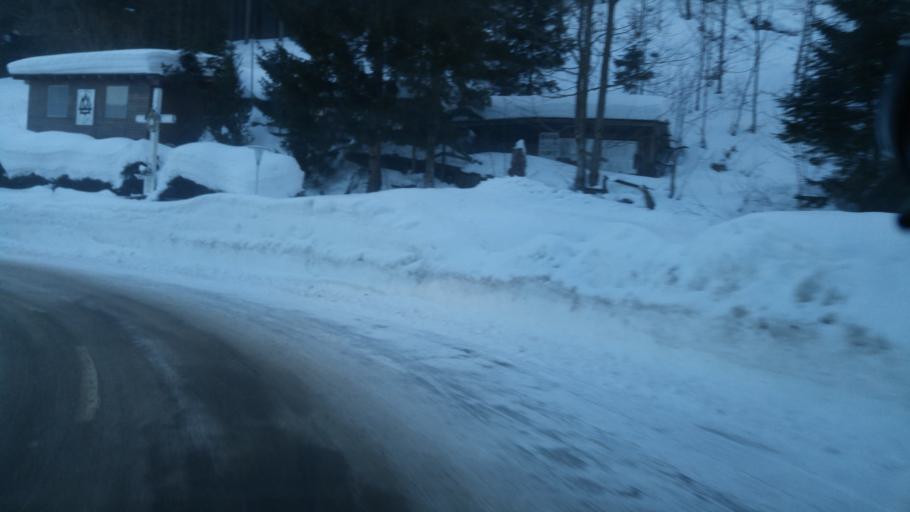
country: AT
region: Lower Austria
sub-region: Politischer Bezirk Wiener Neustadt
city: Rohr im Gebirge
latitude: 47.8880
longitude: 15.6815
